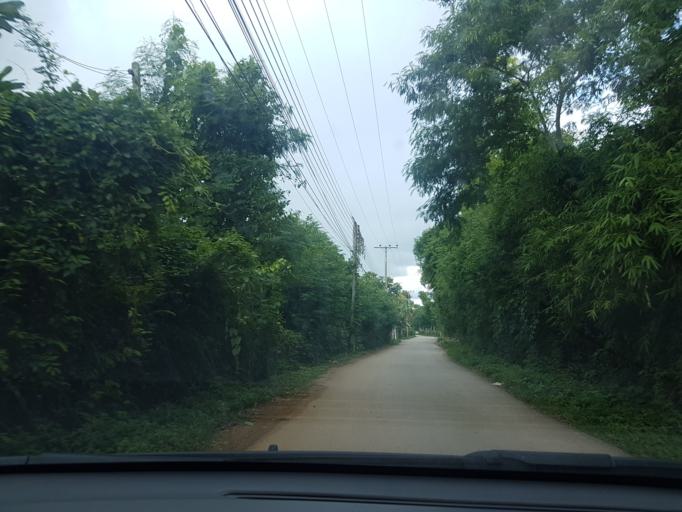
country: TH
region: Lampang
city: Ko Kha
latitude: 18.2218
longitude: 99.4170
